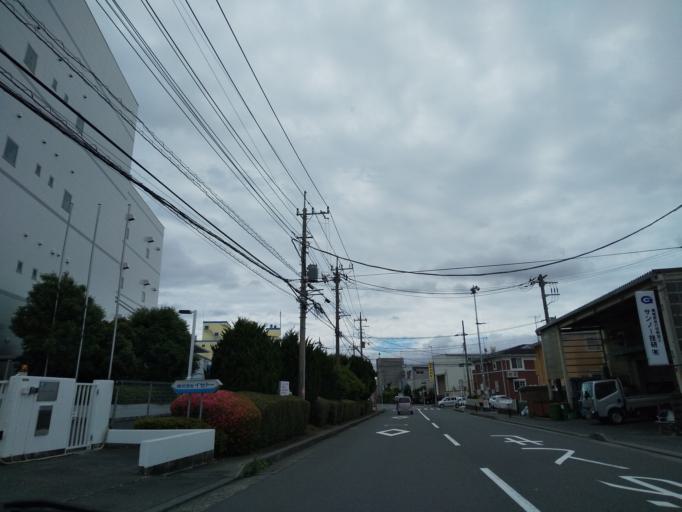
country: JP
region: Kanagawa
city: Zama
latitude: 35.5198
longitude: 139.3390
